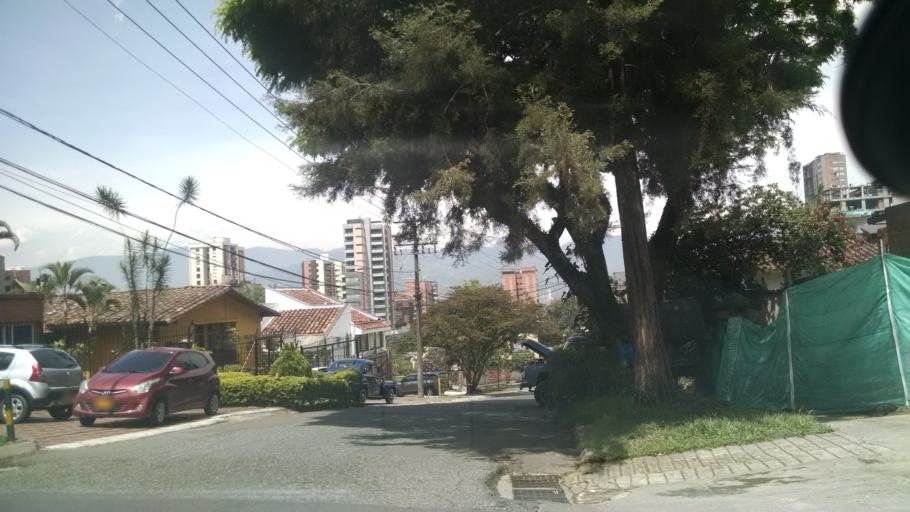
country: CO
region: Antioquia
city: Medellin
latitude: 6.2142
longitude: -75.5619
